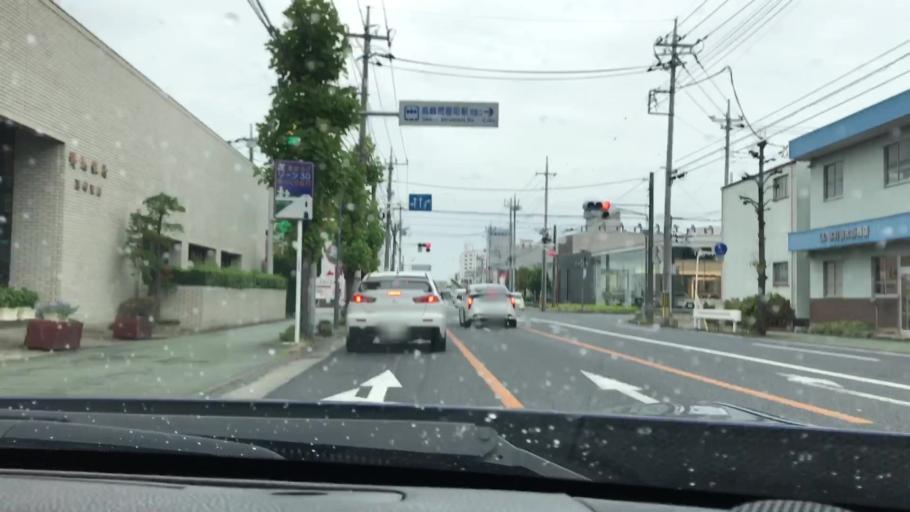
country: JP
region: Gunma
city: Takasaki
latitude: 36.3491
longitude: 139.0145
